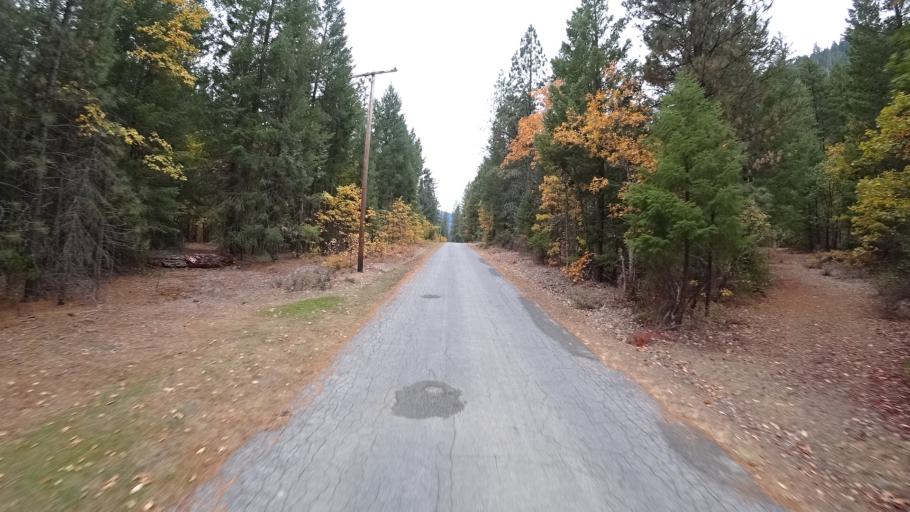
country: US
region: California
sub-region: Siskiyou County
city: Happy Camp
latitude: 41.8800
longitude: -123.4350
